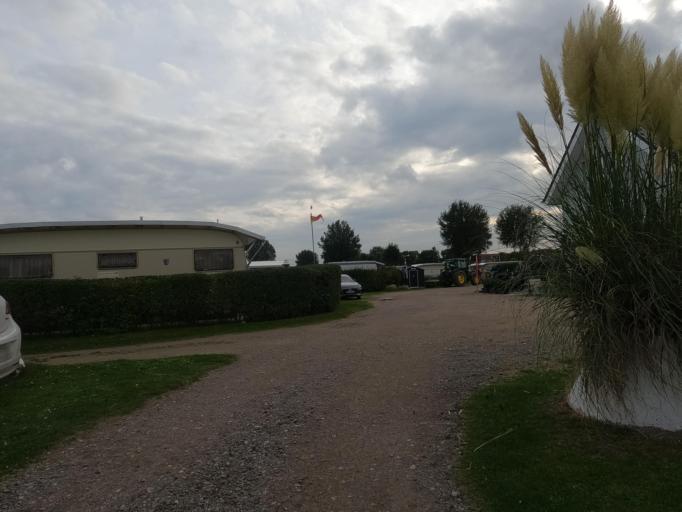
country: DE
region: Schleswig-Holstein
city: Neukirchen
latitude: 54.3271
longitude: 11.0723
